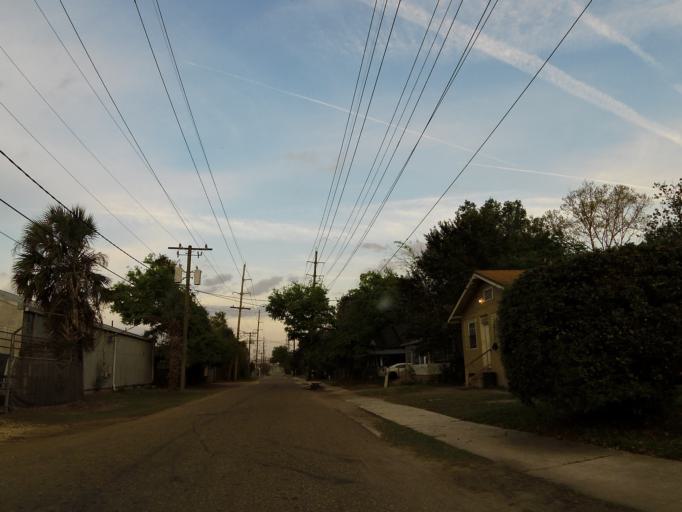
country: US
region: Florida
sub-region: Duval County
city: Jacksonville
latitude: 30.3627
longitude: -81.6313
